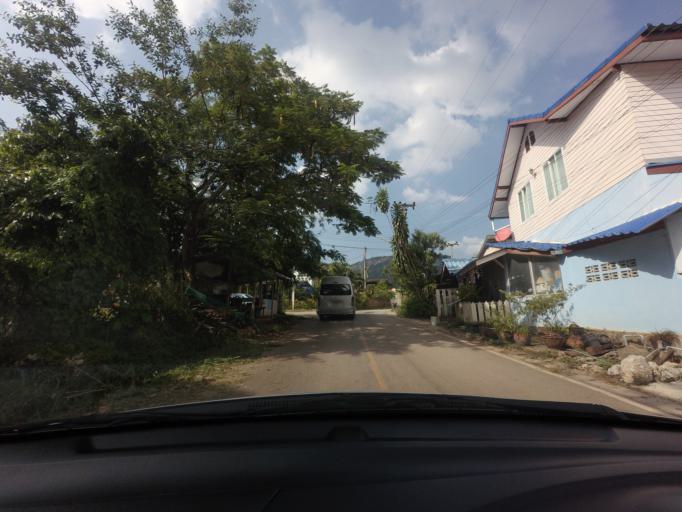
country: TH
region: Nakhon Ratchasima
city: Pak Chong
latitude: 14.5316
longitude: 101.3909
